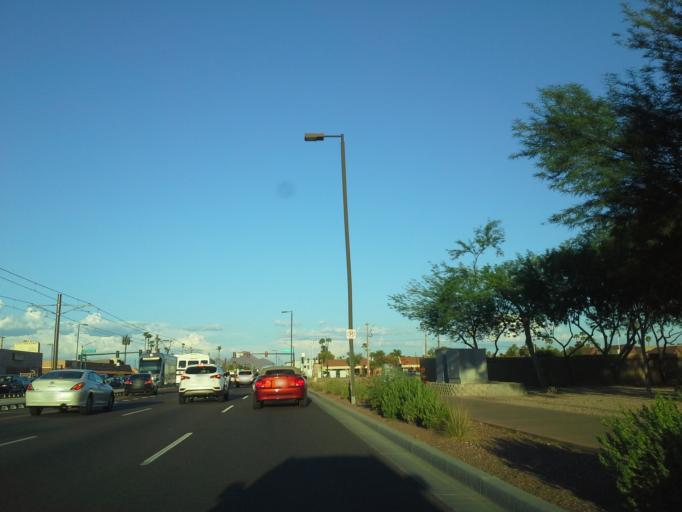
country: US
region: Arizona
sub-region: Maricopa County
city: Phoenix
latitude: 33.5093
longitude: -112.0971
